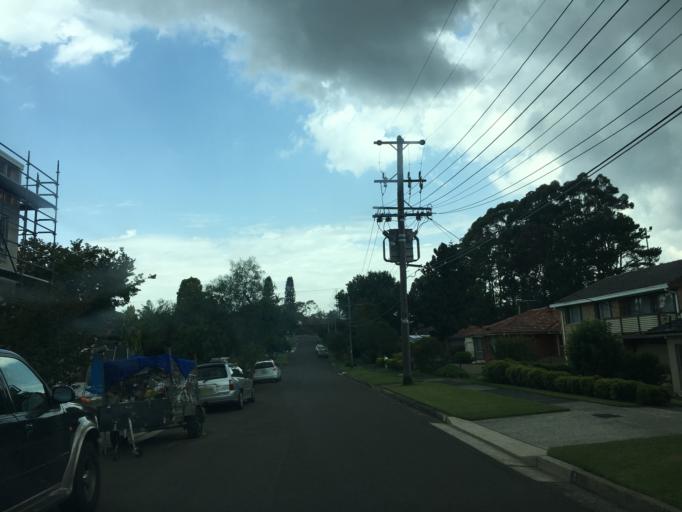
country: AU
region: New South Wales
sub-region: Ryde
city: Marsfield
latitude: -33.7756
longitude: 151.0994
